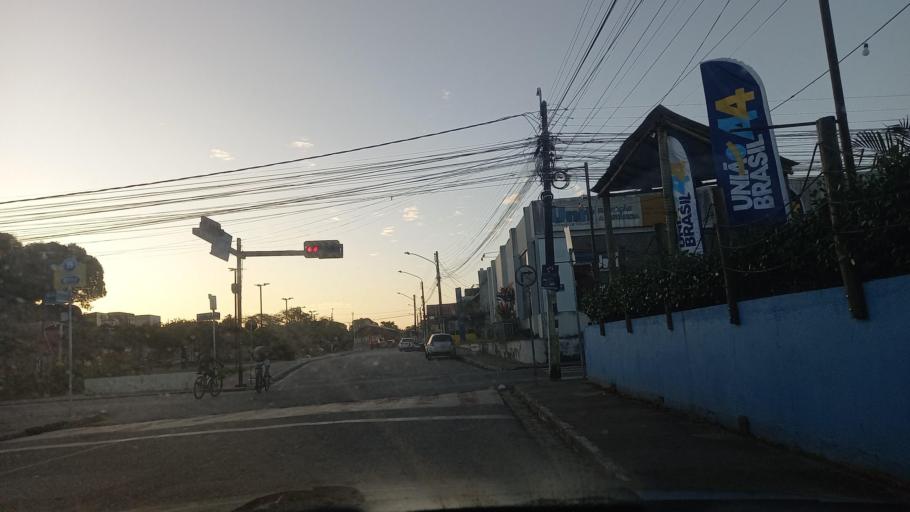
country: BR
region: Alagoas
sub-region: Arapiraca
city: Arapiraca
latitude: -9.7528
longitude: -36.6561
